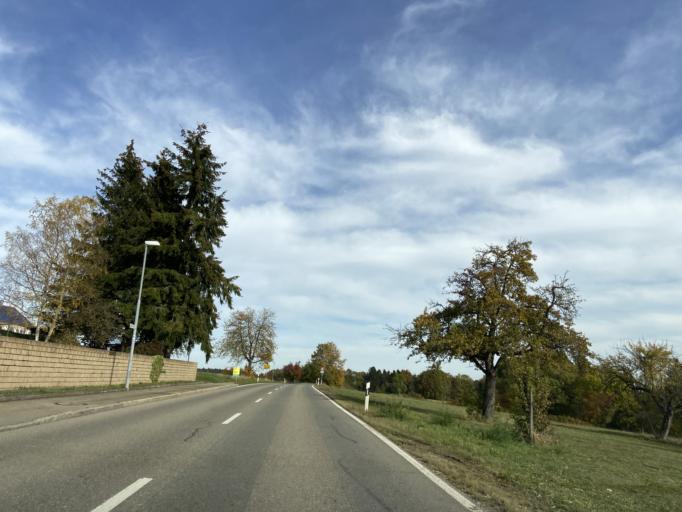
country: DE
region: Baden-Wuerttemberg
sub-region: Tuebingen Region
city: Schwenningen
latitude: 48.1160
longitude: 9.0304
